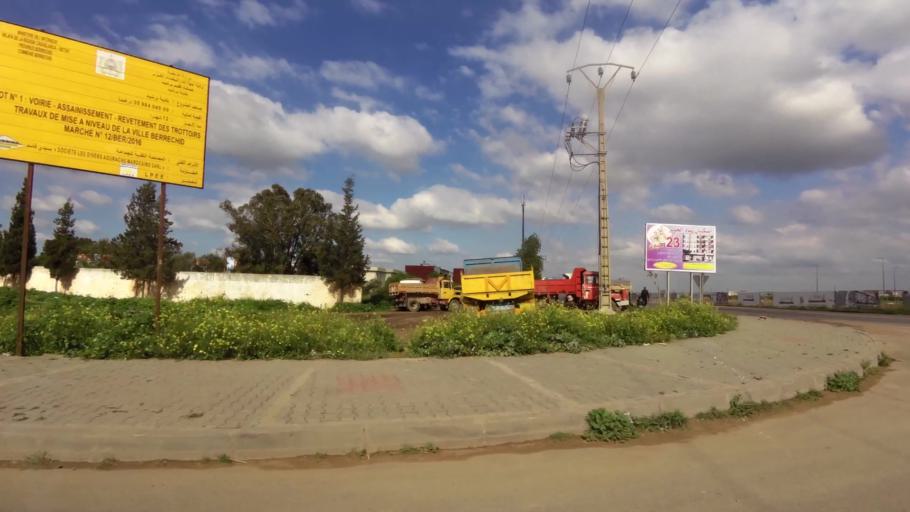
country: MA
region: Chaouia-Ouardigha
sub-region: Settat Province
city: Berrechid
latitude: 33.2692
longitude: -7.5683
